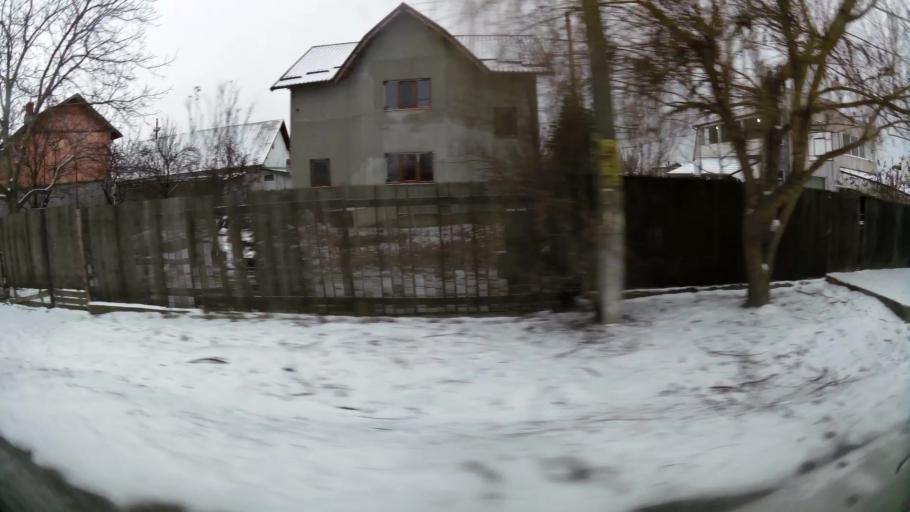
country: RO
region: Prahova
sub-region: Comuna Berceni
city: Corlatesti
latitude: 44.9267
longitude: 26.0689
